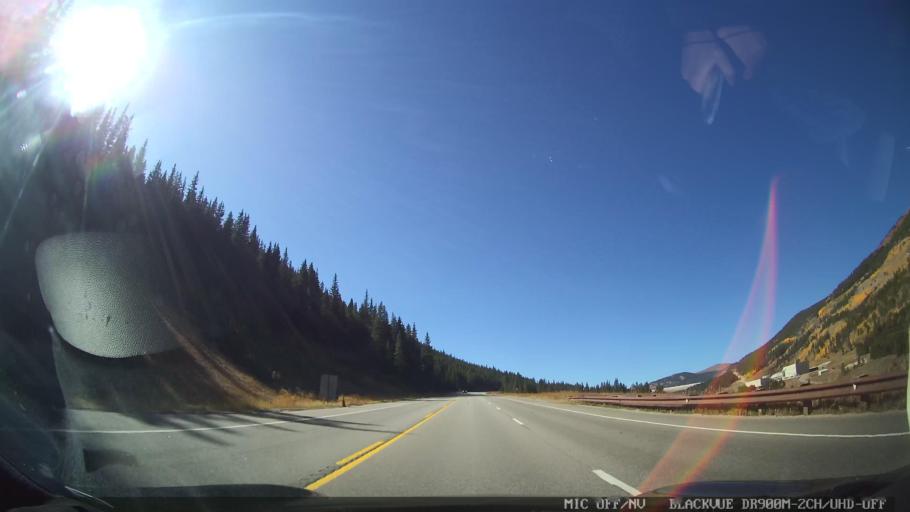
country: US
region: Colorado
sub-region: Summit County
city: Breckenridge
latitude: 39.4536
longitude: -106.1467
